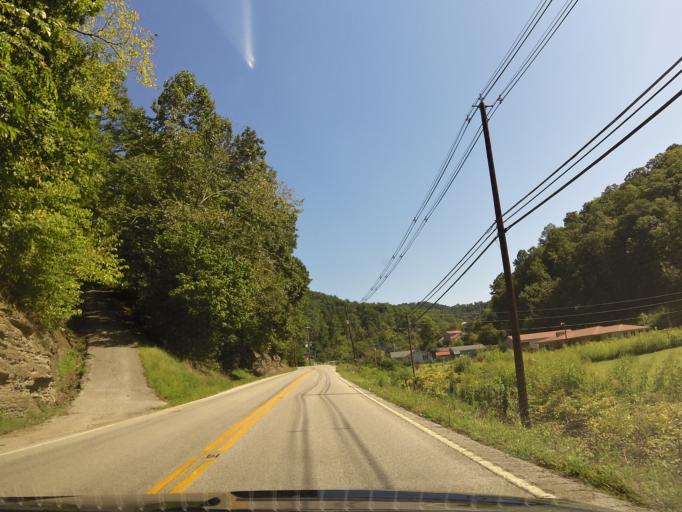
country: US
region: Kentucky
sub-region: Clay County
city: Manchester
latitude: 37.0923
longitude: -83.6704
